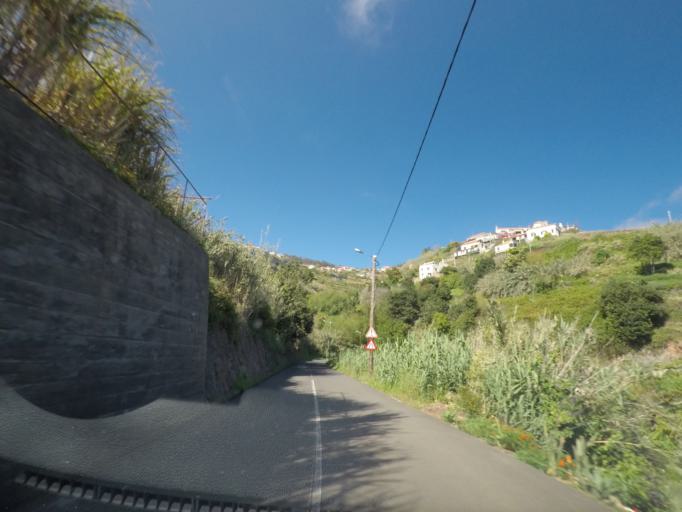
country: PT
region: Madeira
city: Ponta do Sol
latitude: 32.6964
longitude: -17.1012
